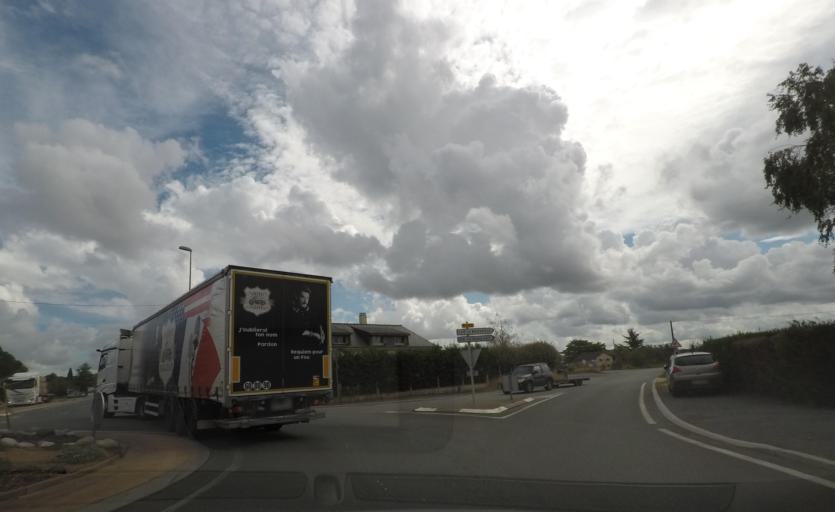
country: FR
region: Pays de la Loire
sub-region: Departement de Maine-et-Loire
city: Corze
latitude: 47.5541
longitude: -0.3823
